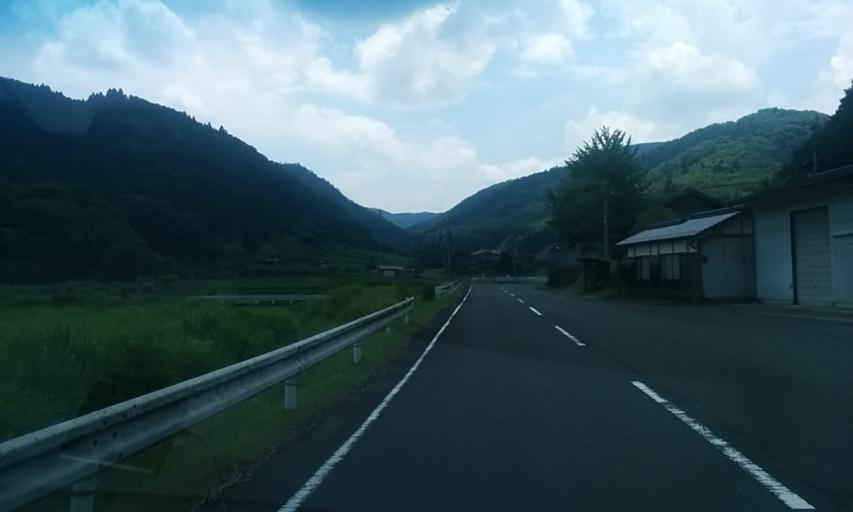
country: JP
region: Kyoto
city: Ayabe
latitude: 35.1948
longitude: 135.2171
